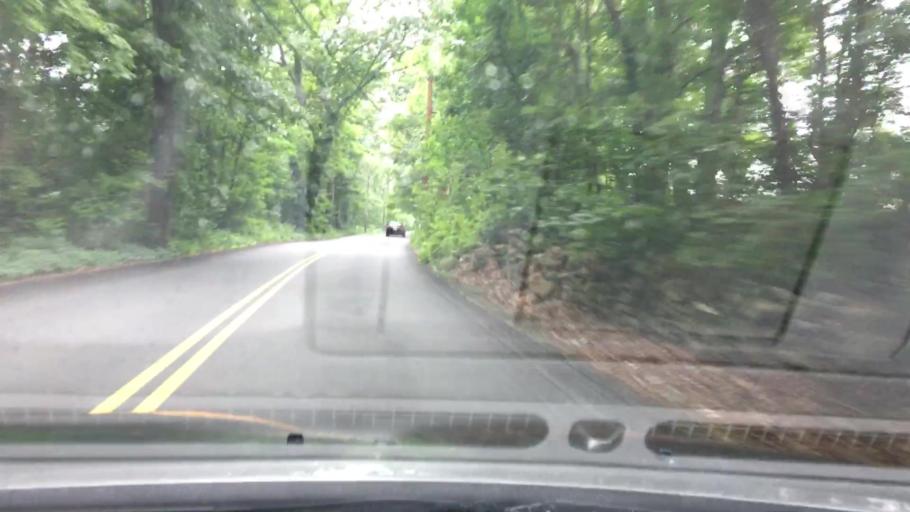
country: US
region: Rhode Island
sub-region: Providence County
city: Cumberland Hill
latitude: 42.0229
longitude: -71.4525
